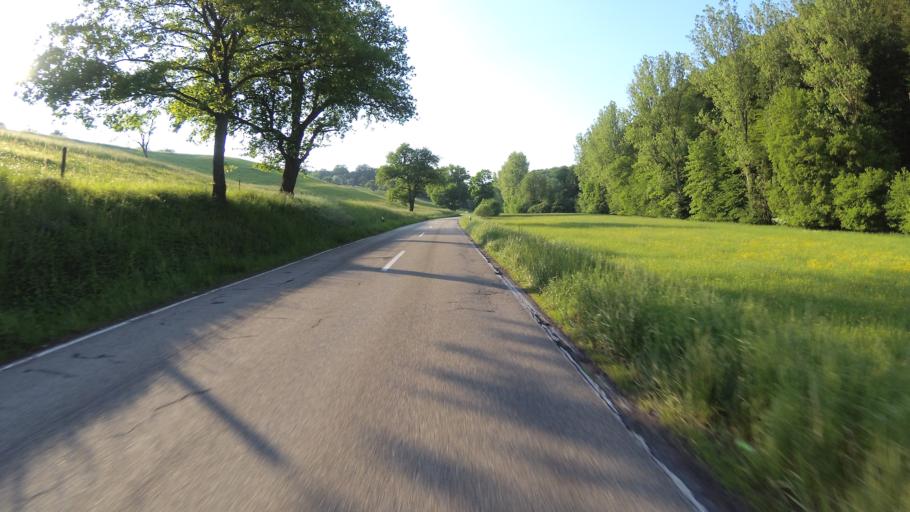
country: DE
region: Rheinland-Pfalz
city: Dietrichingen
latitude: 49.2092
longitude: 7.4256
